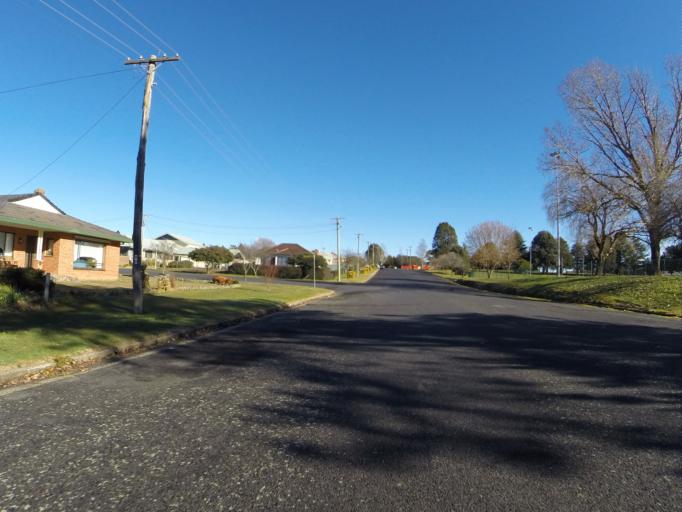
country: AU
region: New South Wales
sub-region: Oberon
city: Oberon
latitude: -33.7015
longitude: 149.8568
